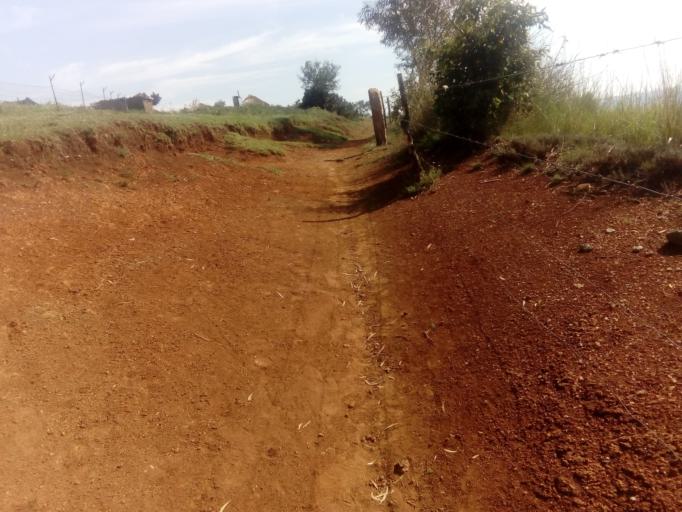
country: LS
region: Berea
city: Teyateyaneng
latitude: -29.2287
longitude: 27.8707
